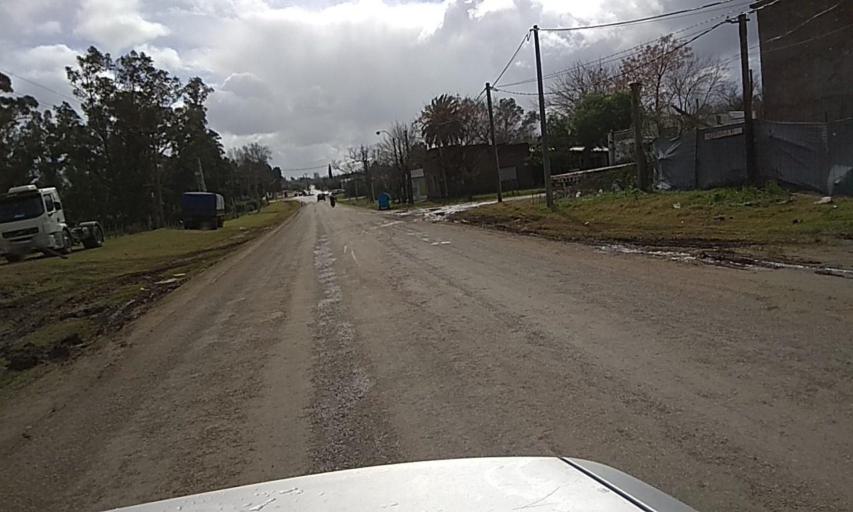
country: UY
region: Florida
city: Florida
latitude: -34.1071
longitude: -56.2237
